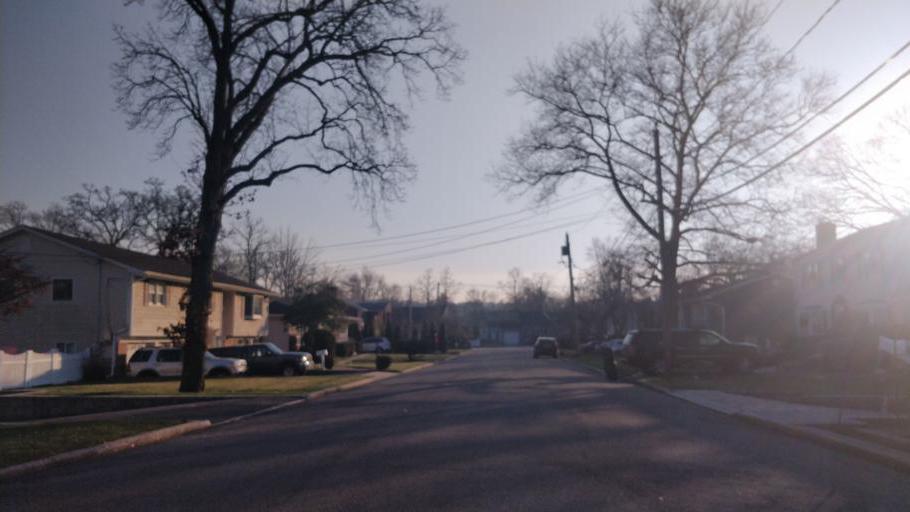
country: US
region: New York
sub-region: Nassau County
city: Bayville
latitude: 40.9101
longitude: -73.5566
